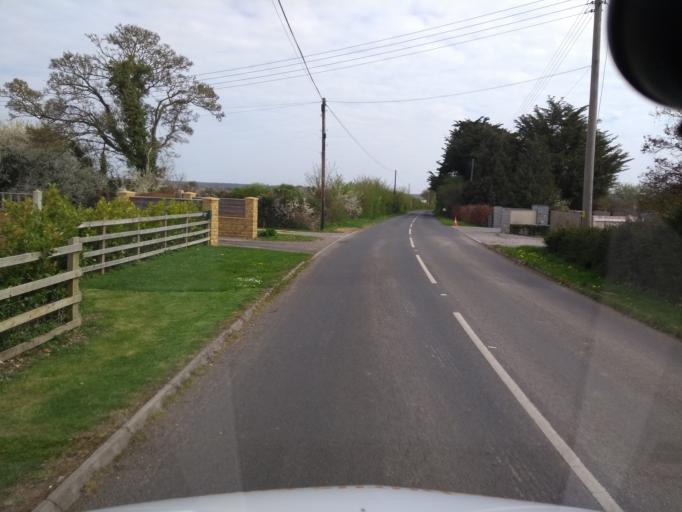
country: GB
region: England
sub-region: Somerset
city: Martock
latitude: 51.0388
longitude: -2.7481
